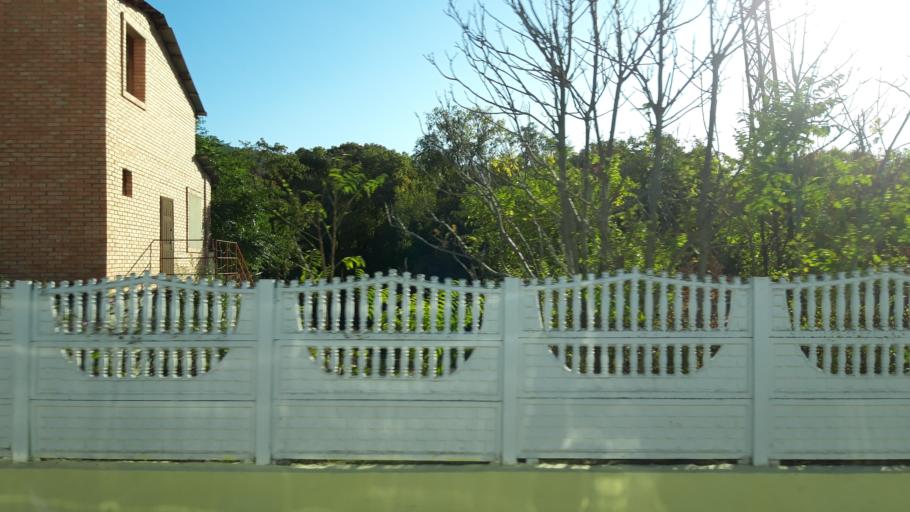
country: RU
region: Krasnodarskiy
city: Kabardinka
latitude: 44.6475
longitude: 37.9378
